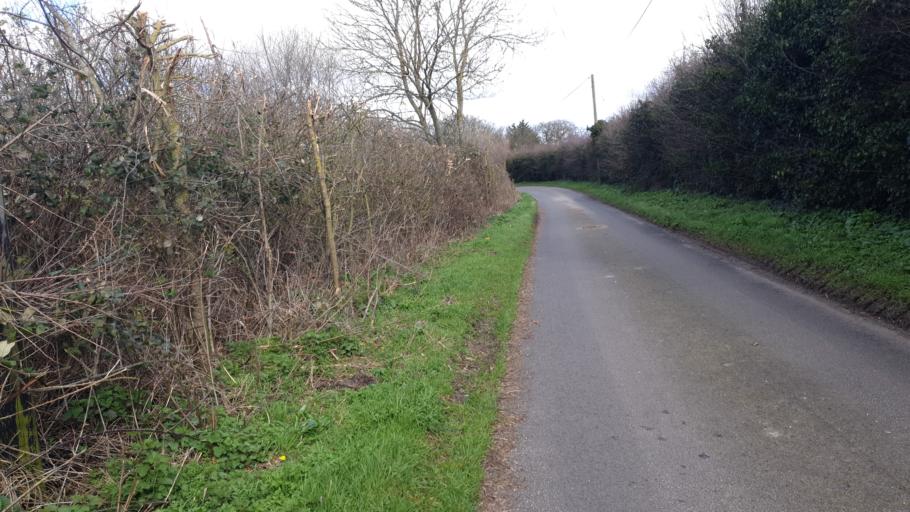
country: GB
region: England
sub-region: Essex
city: Little Clacton
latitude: 51.8270
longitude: 1.1731
